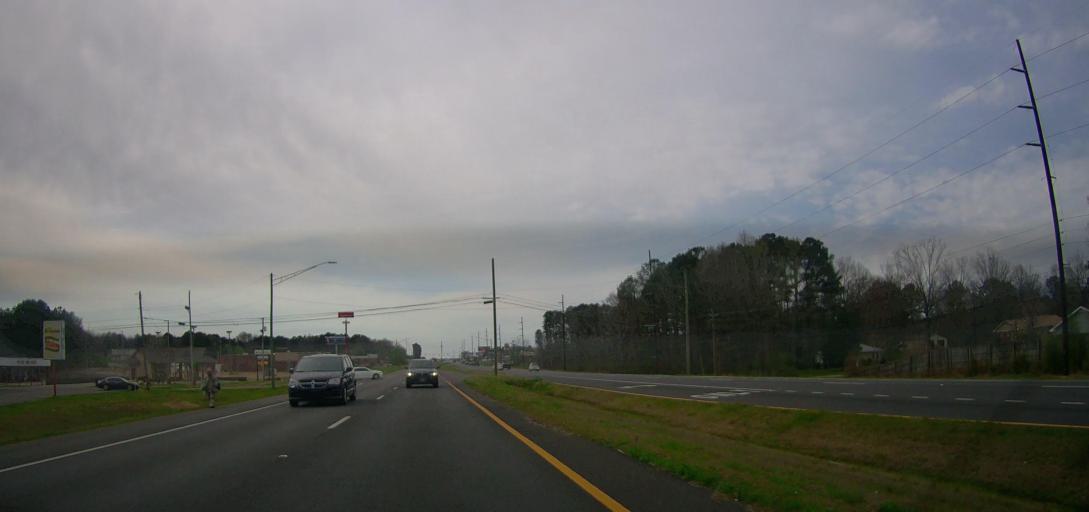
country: US
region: Alabama
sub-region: Walker County
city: Jasper
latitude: 33.8436
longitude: -87.2481
